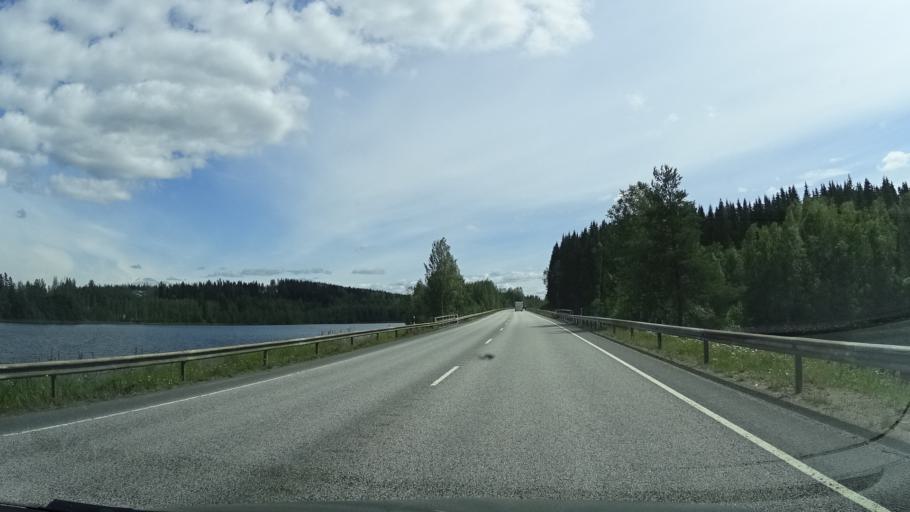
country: FI
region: Central Finland
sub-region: Jyvaeskylae
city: Jyvaeskylae
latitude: 62.2571
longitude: 25.6149
